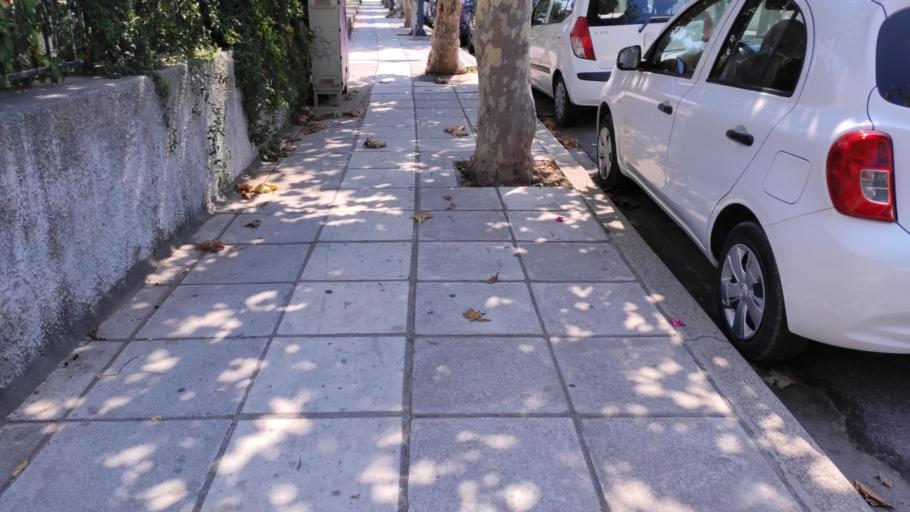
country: GR
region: South Aegean
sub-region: Nomos Dodekanisou
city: Kos
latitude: 36.8939
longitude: 27.2852
